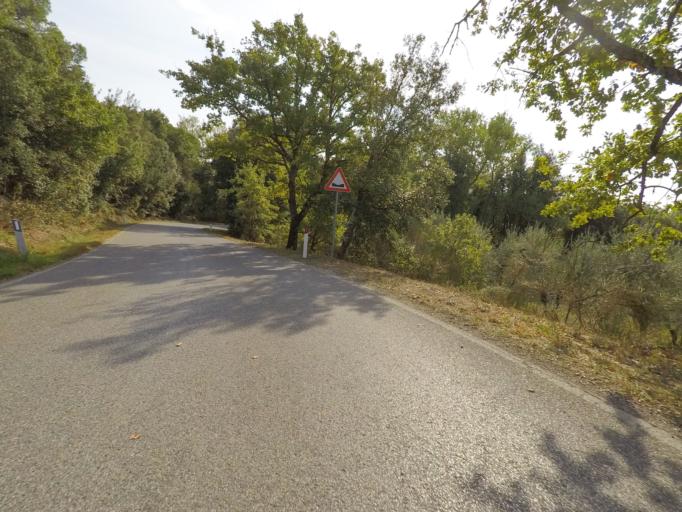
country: IT
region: Tuscany
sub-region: Provincia di Siena
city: Belverde
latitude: 43.4003
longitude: 11.3522
